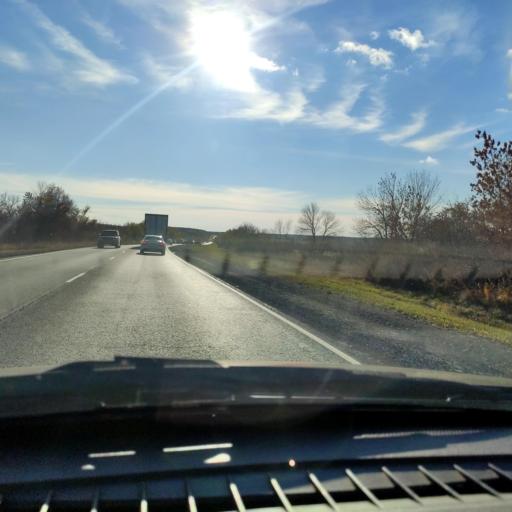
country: RU
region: Samara
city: Zhigulevsk
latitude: 53.3036
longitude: 49.3479
